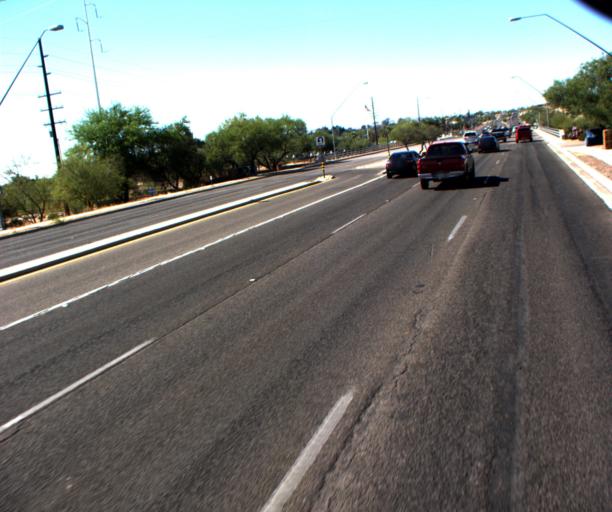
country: US
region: Arizona
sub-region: Pima County
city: Flowing Wells
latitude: 32.2931
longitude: -110.9781
